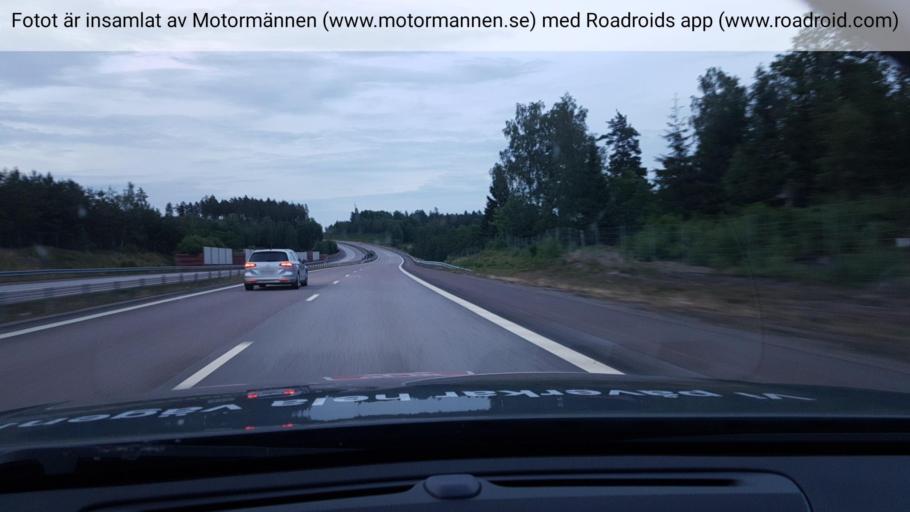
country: SE
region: Soedermanland
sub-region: Nykopings Kommun
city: Olstorp
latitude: 58.7527
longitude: 16.5355
